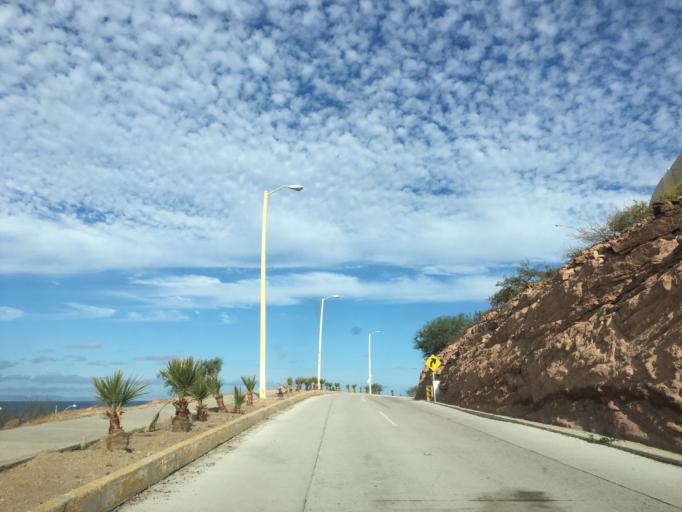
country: MX
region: Baja California Sur
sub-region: La Paz
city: La Paz
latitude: 24.1972
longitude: -110.2995
